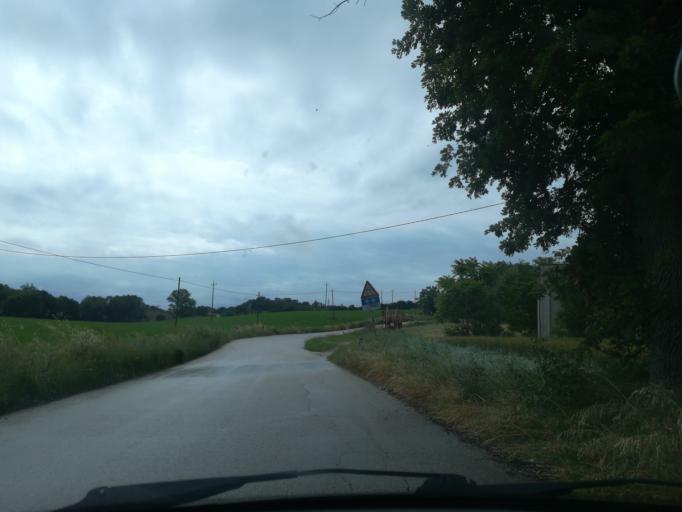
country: IT
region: The Marches
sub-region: Provincia di Macerata
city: Petriolo
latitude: 43.2312
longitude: 13.4618
